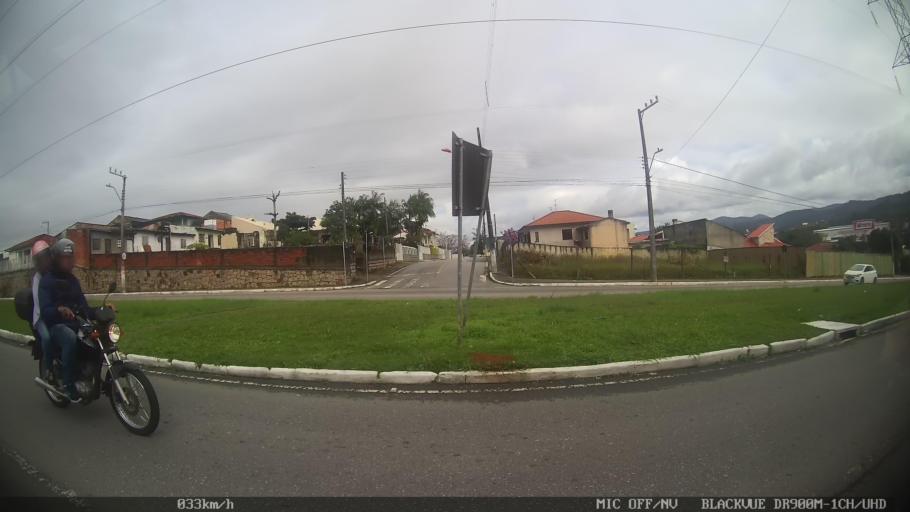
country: BR
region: Santa Catarina
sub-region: Sao Jose
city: Campinas
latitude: -27.5633
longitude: -48.6357
